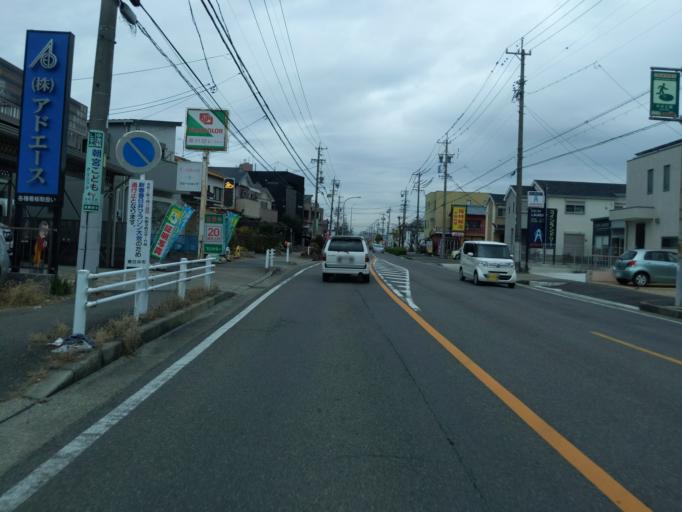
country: JP
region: Aichi
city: Kasugai
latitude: 35.2483
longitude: 136.9652
